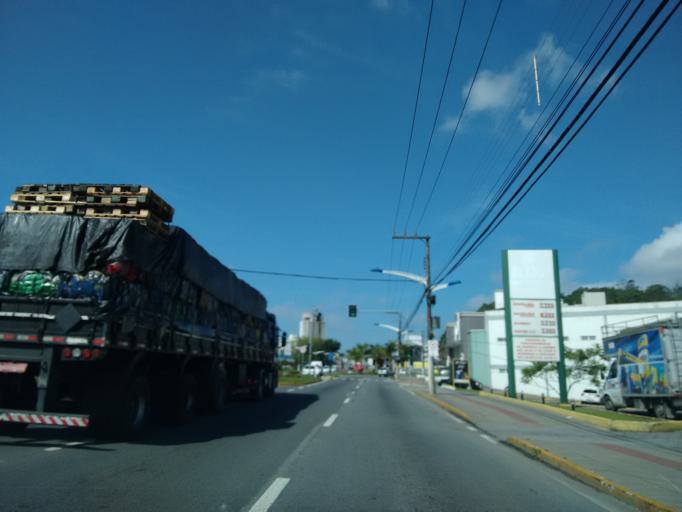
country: BR
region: Santa Catarina
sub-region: Itajai
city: Itajai
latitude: -26.9308
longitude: -48.6865
